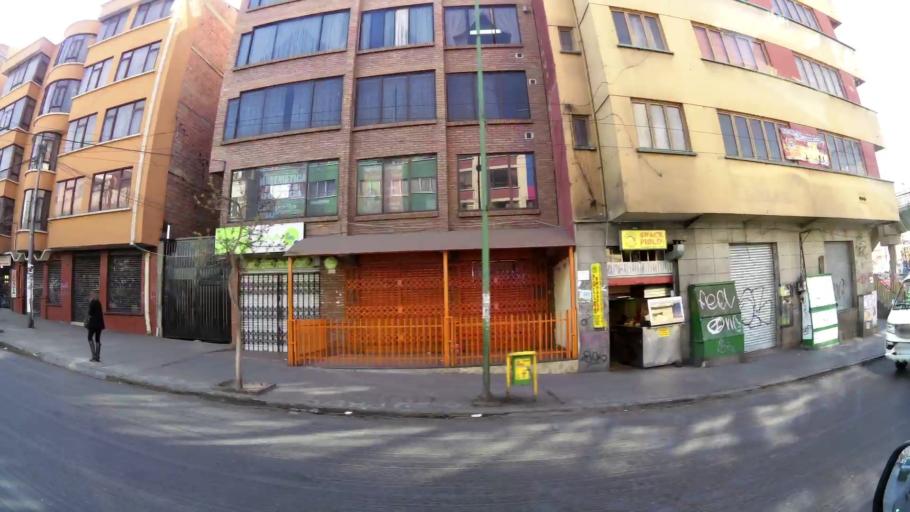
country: BO
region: La Paz
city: La Paz
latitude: -16.4997
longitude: -68.1249
